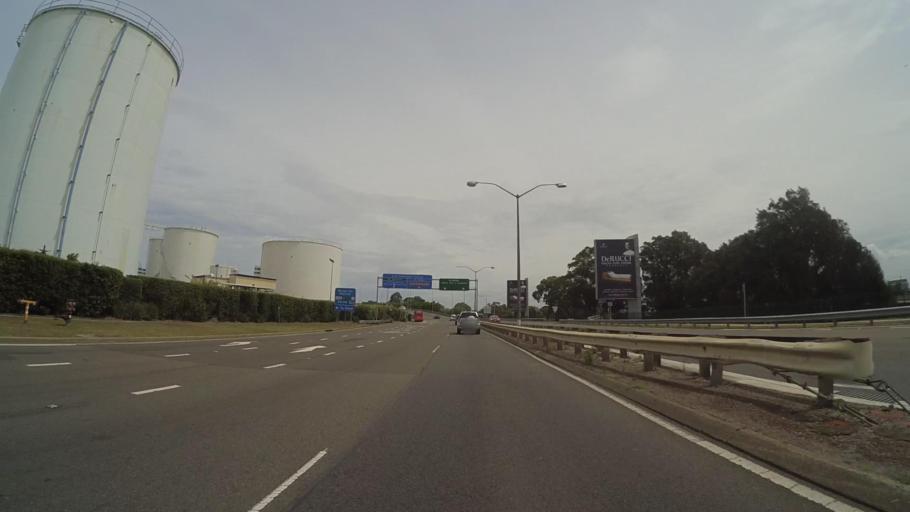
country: AU
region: New South Wales
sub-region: Rockdale
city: Arncliffe
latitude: -33.9302
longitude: 151.1648
